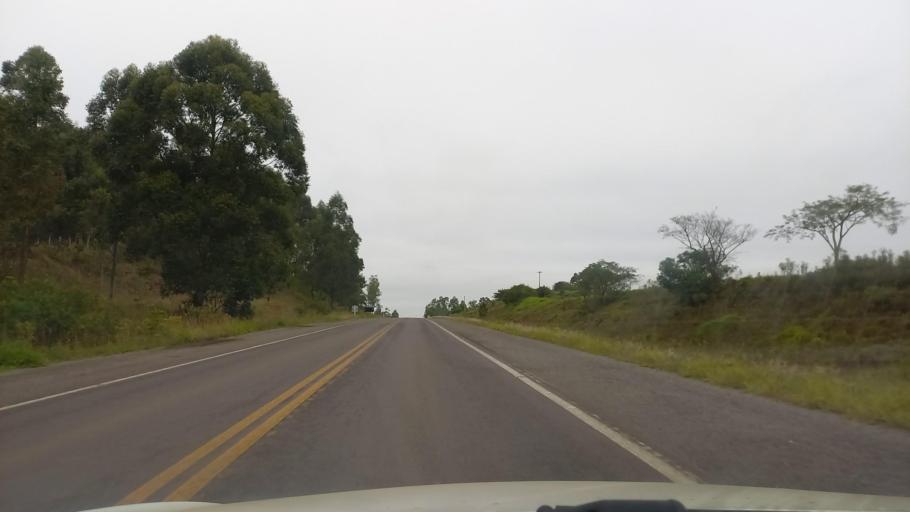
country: BR
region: Rio Grande do Sul
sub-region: Sao Pedro Do Sul
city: Sao Pedro do Sul
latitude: -29.7726
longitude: -54.0960
